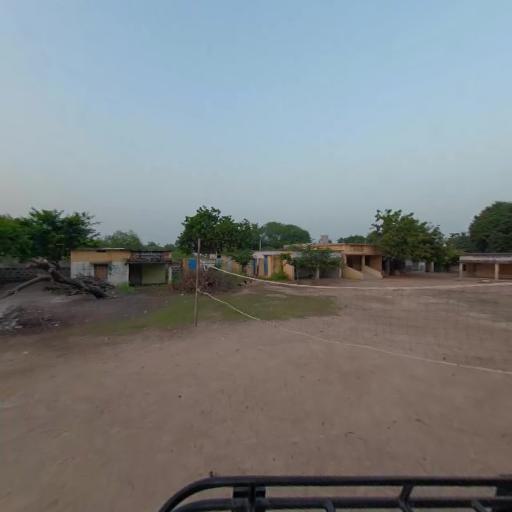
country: IN
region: Telangana
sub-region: Nalgonda
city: Suriapet
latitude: 17.1043
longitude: 79.5290
